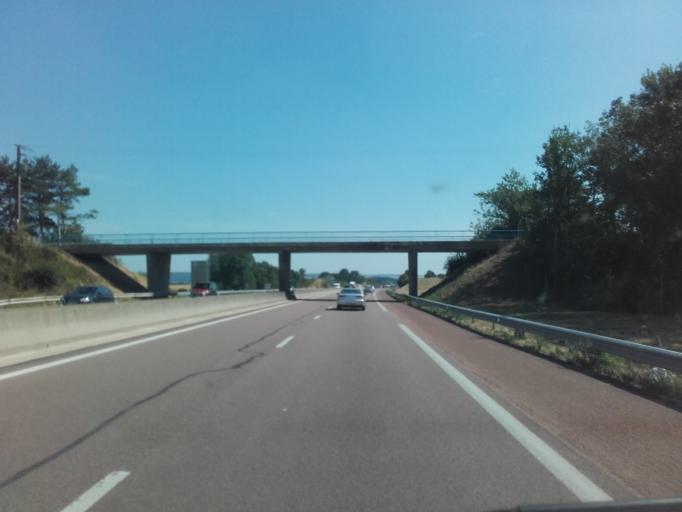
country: FR
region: Bourgogne
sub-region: Departement de la Cote-d'Or
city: Pouilly-en-Auxois
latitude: 47.2419
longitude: 4.5774
